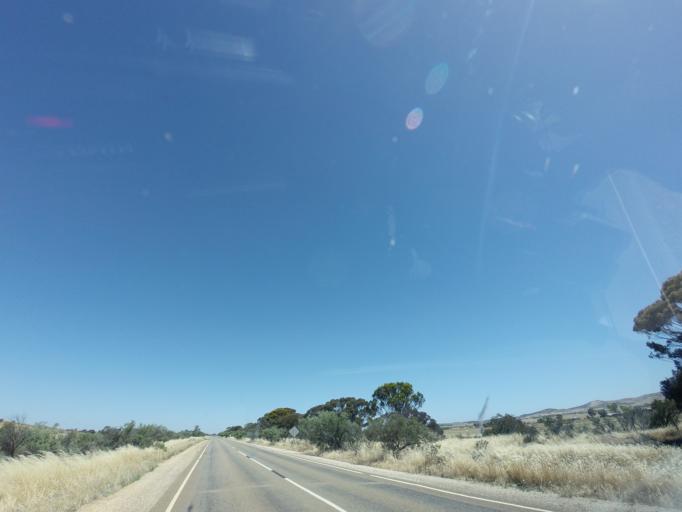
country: AU
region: South Australia
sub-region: Peterborough
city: Peterborough
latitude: -32.7853
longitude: 138.6704
